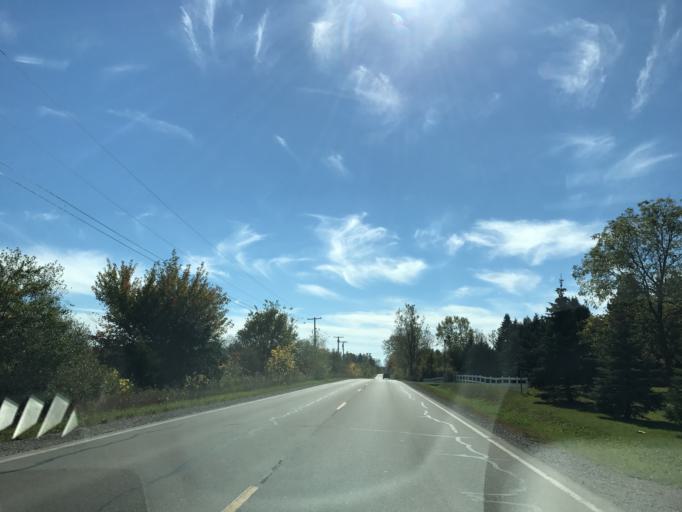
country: US
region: Michigan
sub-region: Oakland County
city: South Lyon
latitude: 42.4005
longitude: -83.6457
